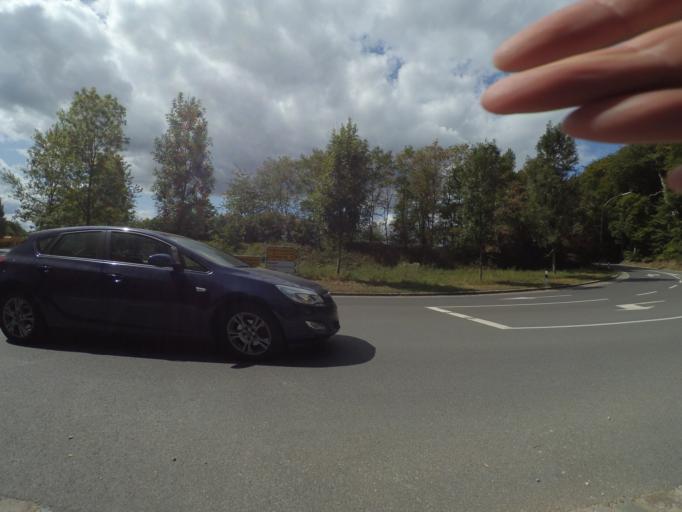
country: LU
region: Luxembourg
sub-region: Canton de Luxembourg
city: Niederanven
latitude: 49.6587
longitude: 6.2272
